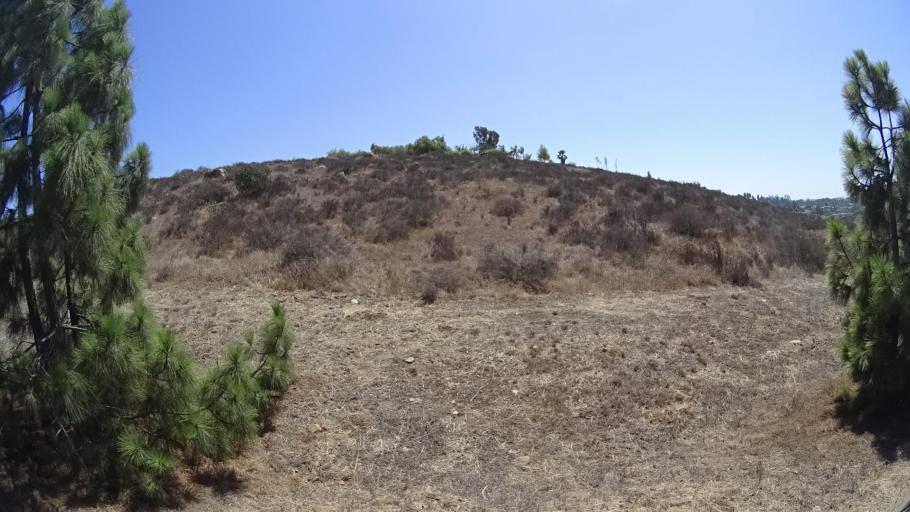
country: US
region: California
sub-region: San Diego County
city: Rancho Santa Fe
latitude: 33.0201
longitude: -117.1740
